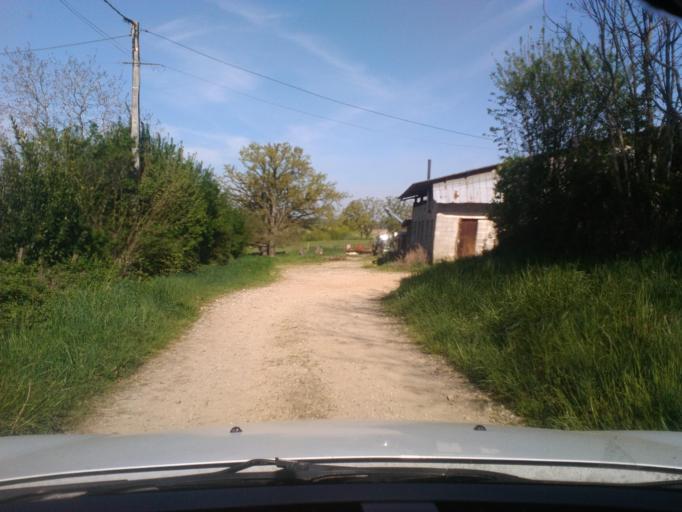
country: FR
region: Rhone-Alpes
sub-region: Departement de l'Ain
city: Coligny
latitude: 46.3473
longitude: 5.3203
